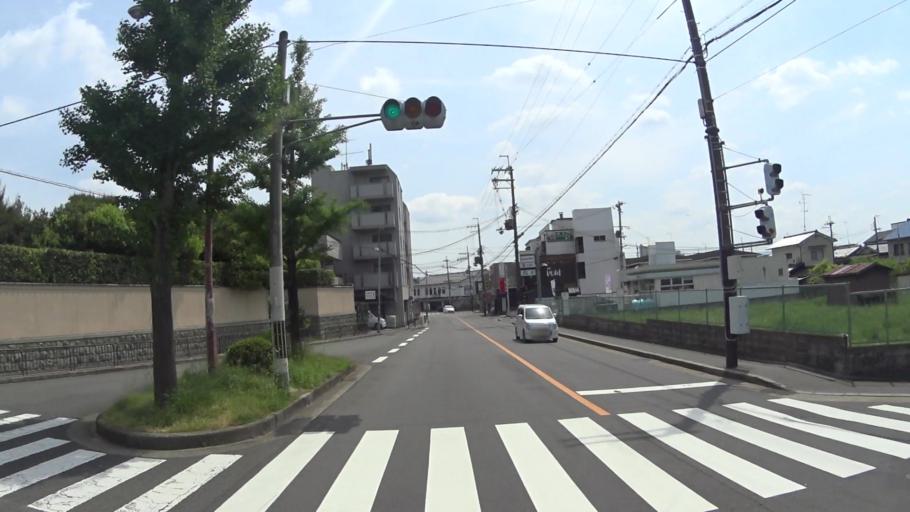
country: JP
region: Kyoto
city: Kyoto
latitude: 35.0349
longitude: 135.7261
